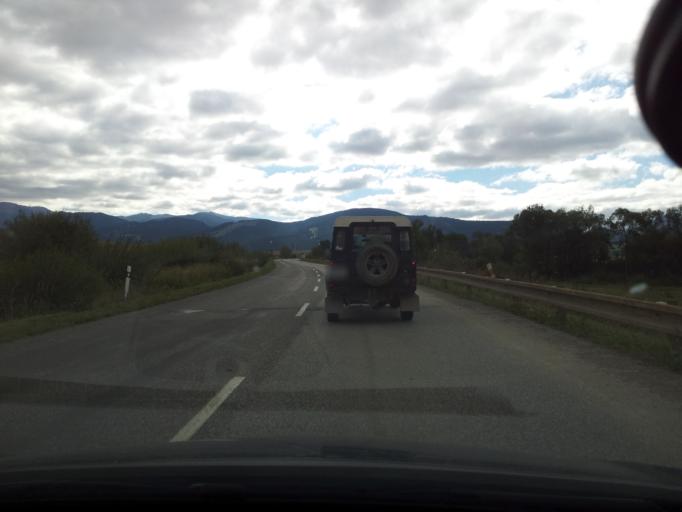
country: SK
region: Zilinsky
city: Ruzomberok
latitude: 49.0777
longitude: 19.4380
